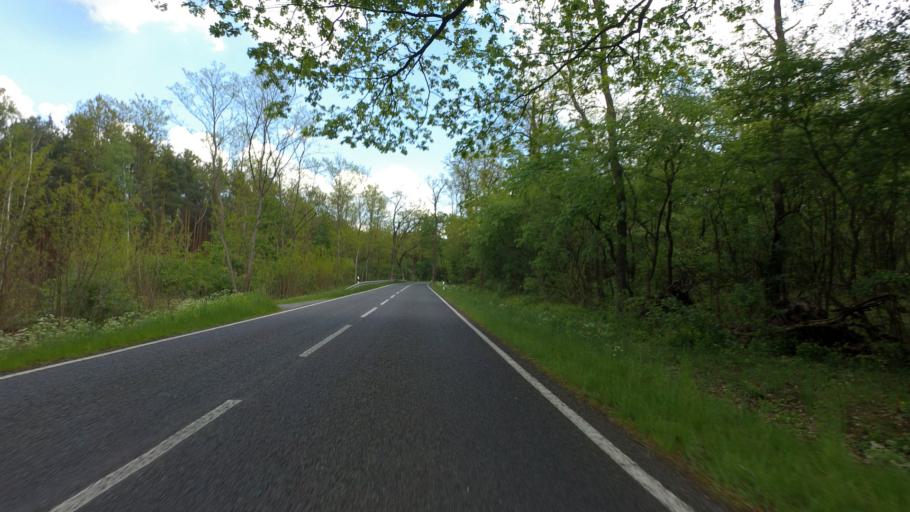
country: DE
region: Brandenburg
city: Straupitz
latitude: 51.9680
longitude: 14.1899
